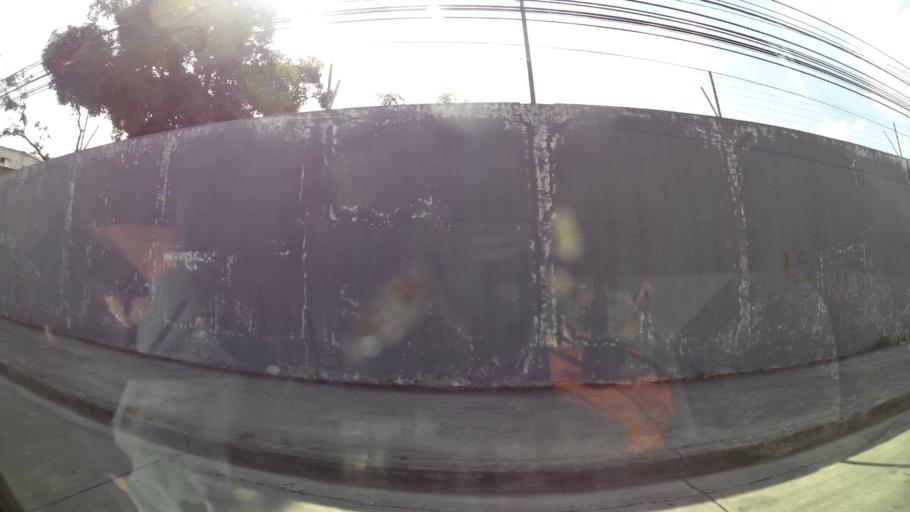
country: EC
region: Guayas
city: Guayaquil
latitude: -2.1563
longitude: -79.9338
